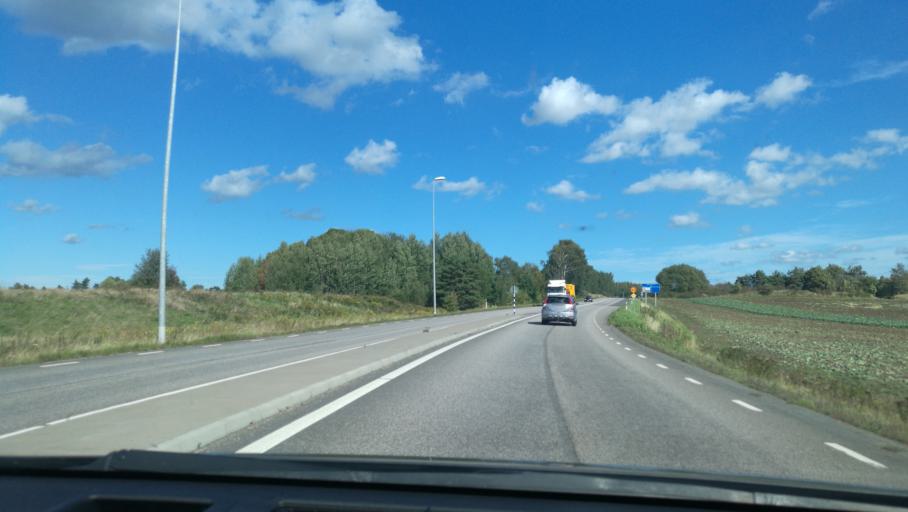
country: SE
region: Vaestra Goetaland
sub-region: Gotene Kommun
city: Kallby
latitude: 58.5009
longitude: 13.3049
